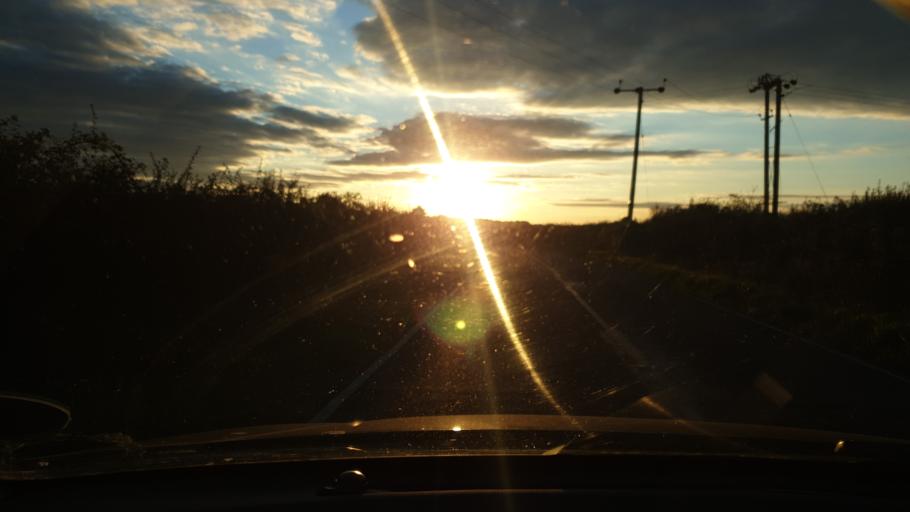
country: GB
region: England
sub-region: Essex
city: Wivenhoe
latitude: 51.9047
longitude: 0.9797
